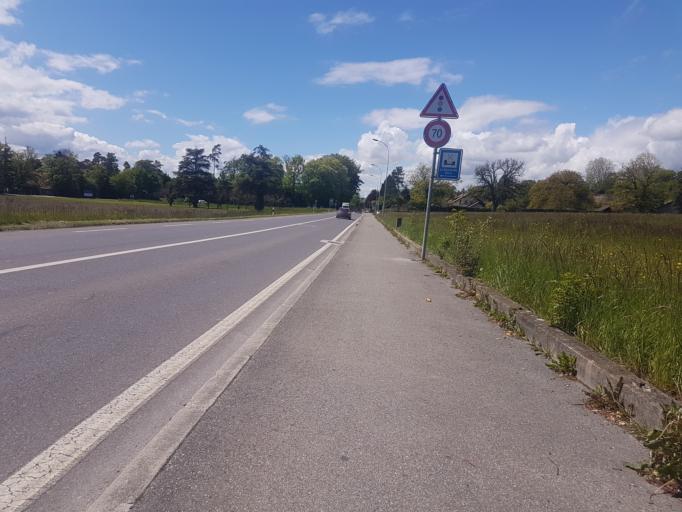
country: CH
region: Vaud
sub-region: Nyon District
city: Prangins
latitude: 46.3957
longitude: 6.2577
